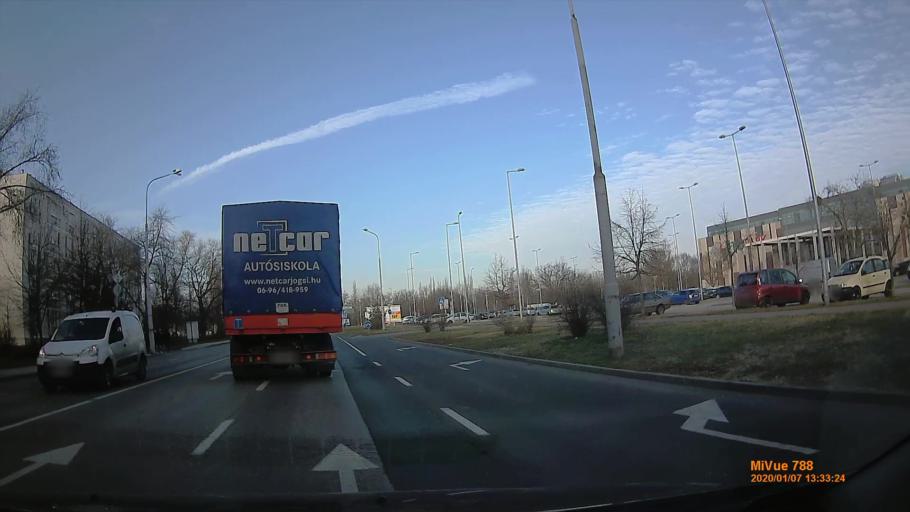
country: HU
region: Gyor-Moson-Sopron
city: Gyor
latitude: 47.6942
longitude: 17.6605
